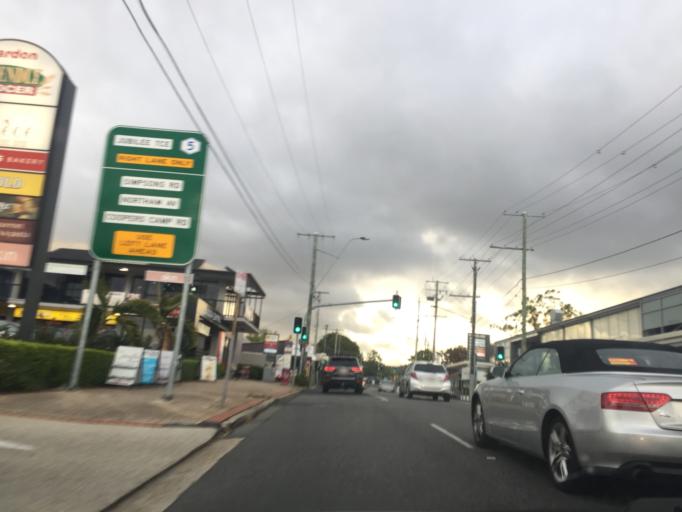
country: AU
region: Queensland
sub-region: Brisbane
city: Milton
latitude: -27.4581
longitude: 152.9871
